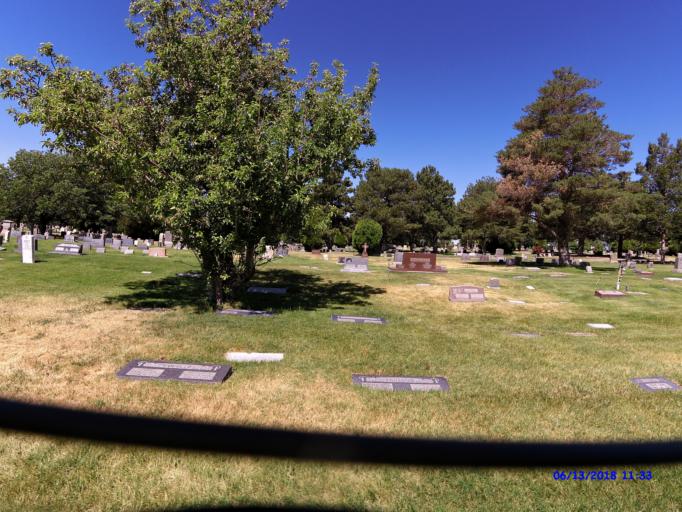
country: US
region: Utah
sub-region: Weber County
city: Ogden
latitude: 41.2337
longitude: -111.9628
